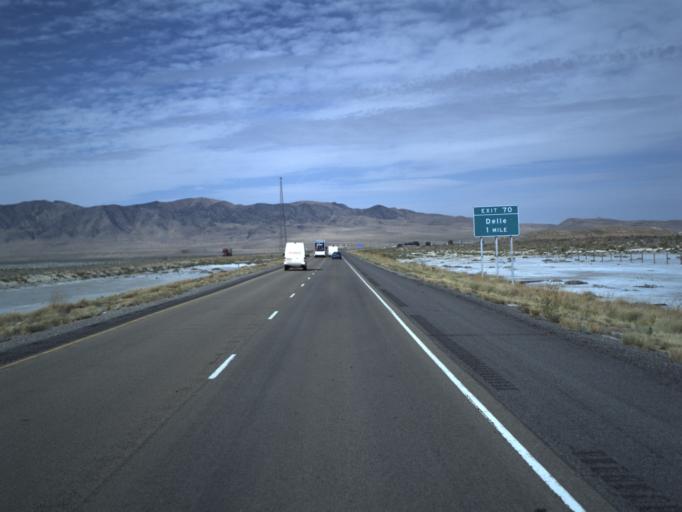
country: US
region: Utah
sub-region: Tooele County
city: Grantsville
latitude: 40.7568
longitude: -112.7596
